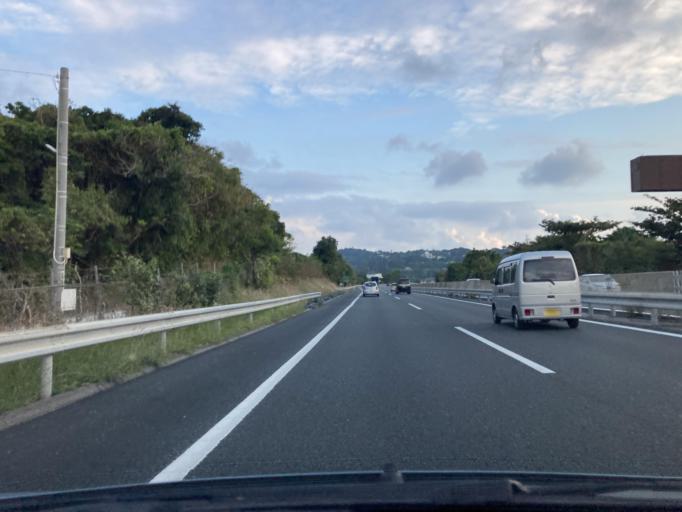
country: JP
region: Okinawa
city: Chatan
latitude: 26.3047
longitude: 127.7903
